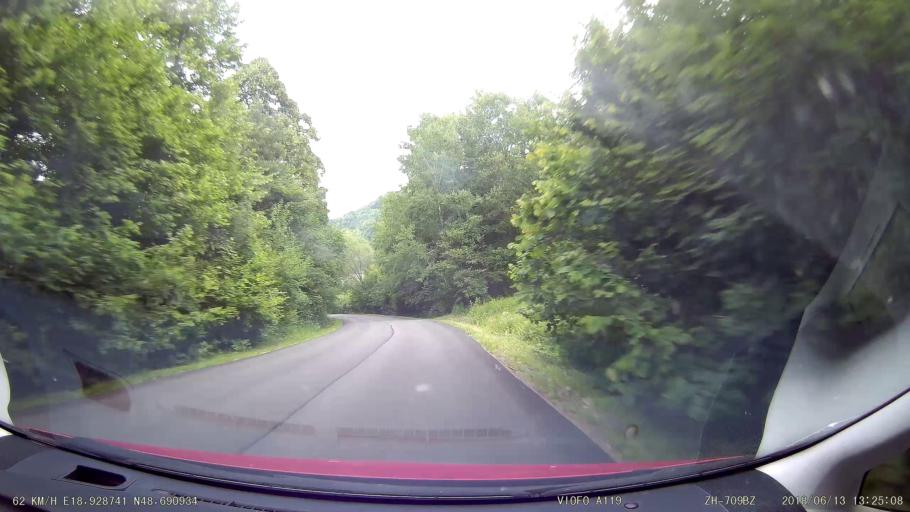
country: SK
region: Banskobystricky
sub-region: Okres Ziar nad Hronom
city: Kremnica
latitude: 48.6910
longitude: 18.9288
